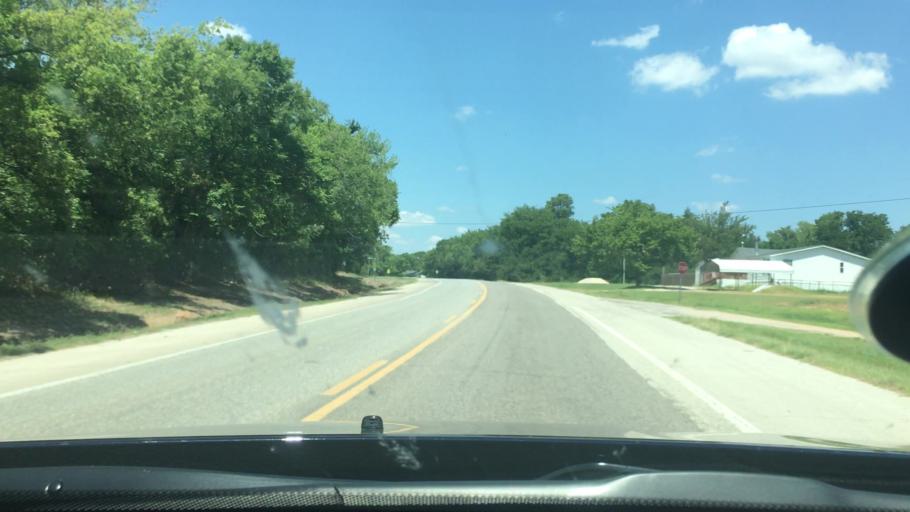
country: US
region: Oklahoma
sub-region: Carter County
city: Dickson
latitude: 34.1848
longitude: -96.8722
